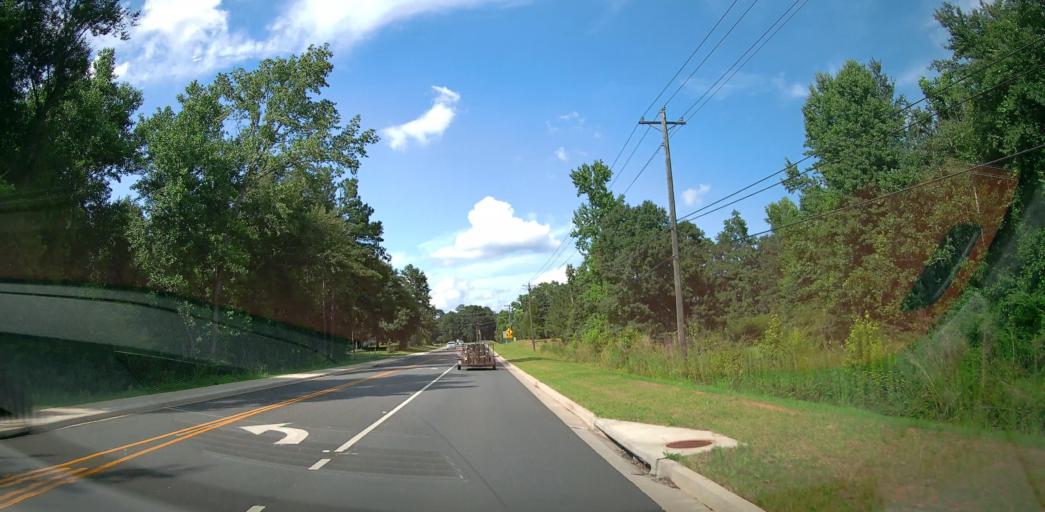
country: US
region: Georgia
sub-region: Houston County
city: Perry
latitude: 32.5135
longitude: -83.6926
